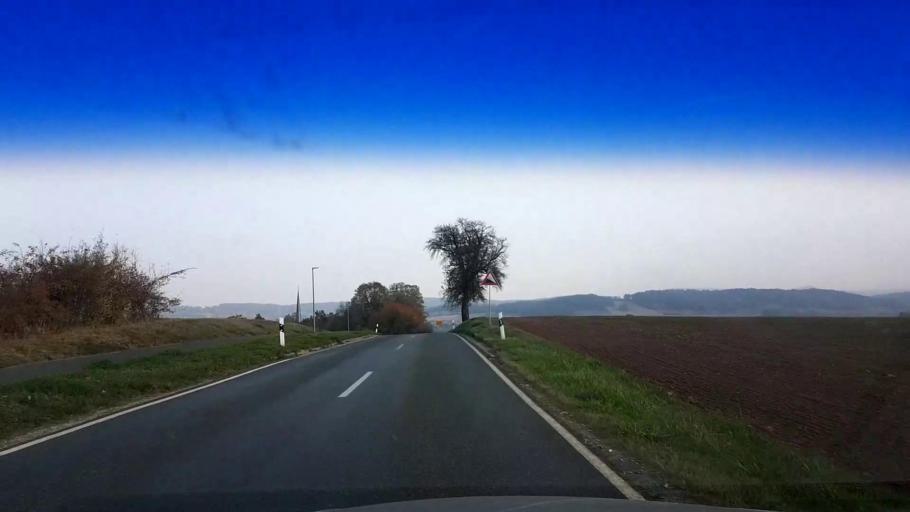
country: DE
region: Bavaria
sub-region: Upper Franconia
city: Altenkunstadt
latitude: 50.1201
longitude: 11.2490
